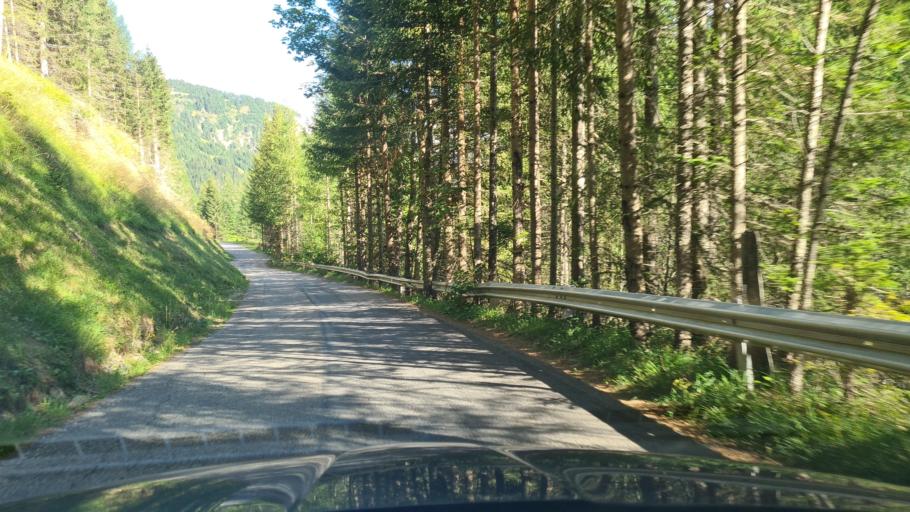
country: AT
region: Salzburg
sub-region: Politischer Bezirk Tamsweg
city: Zederhaus
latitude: 47.1854
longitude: 13.4289
